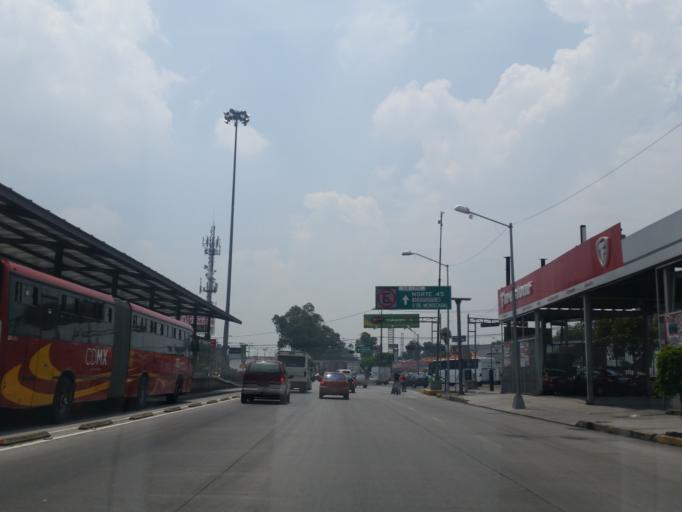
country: MX
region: Mexico
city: Tlalnepantla
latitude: 19.5196
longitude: -99.1638
